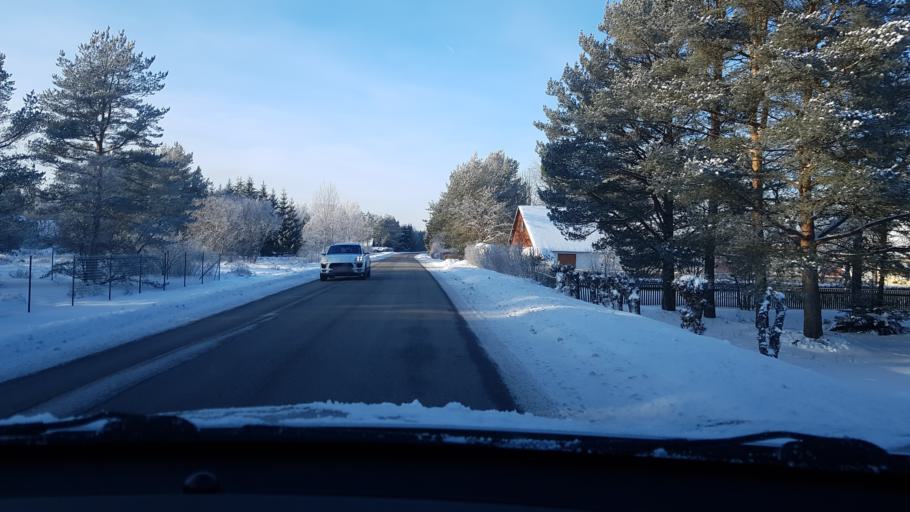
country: EE
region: Harju
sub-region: Harku vald
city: Tabasalu
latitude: 59.3759
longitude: 24.4659
